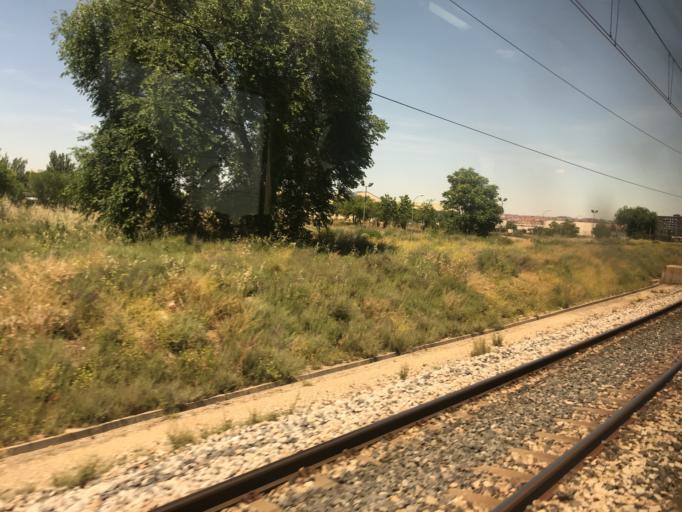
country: ES
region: Madrid
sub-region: Provincia de Madrid
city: Villaverde
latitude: 40.3342
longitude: -3.6878
